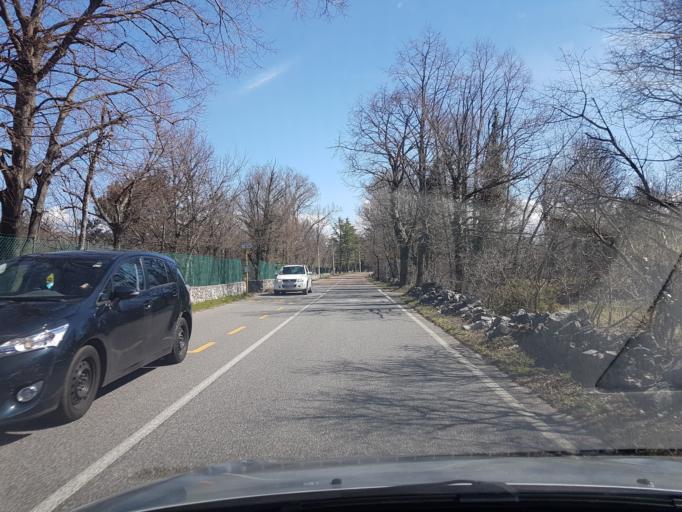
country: IT
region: Friuli Venezia Giulia
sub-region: Provincia di Trieste
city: Domio
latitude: 45.6530
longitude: 13.8469
